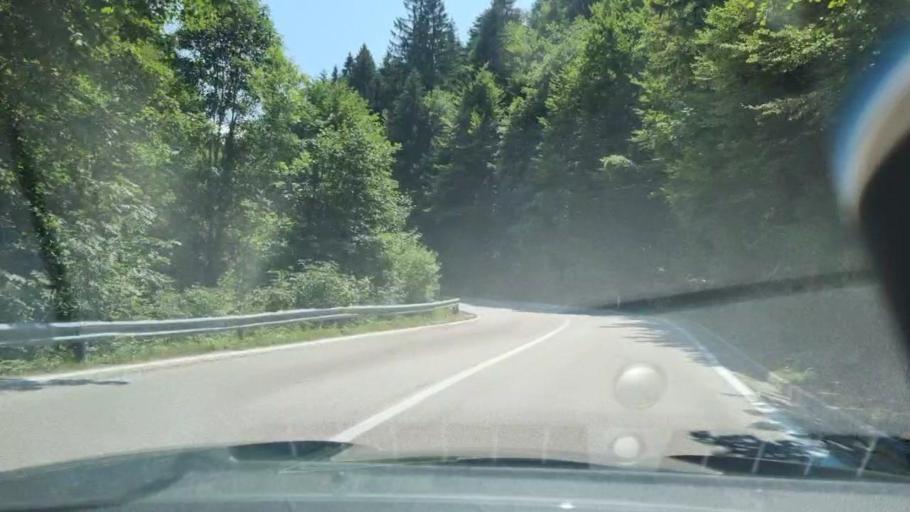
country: BA
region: Federation of Bosnia and Herzegovina
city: Sanica
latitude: 44.5004
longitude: 16.3729
